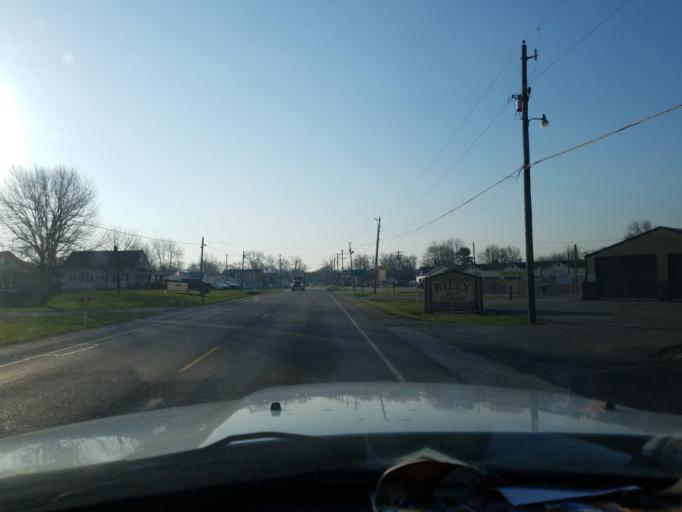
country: US
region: Indiana
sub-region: Vigo County
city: Seelyville
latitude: 39.3933
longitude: -87.3078
